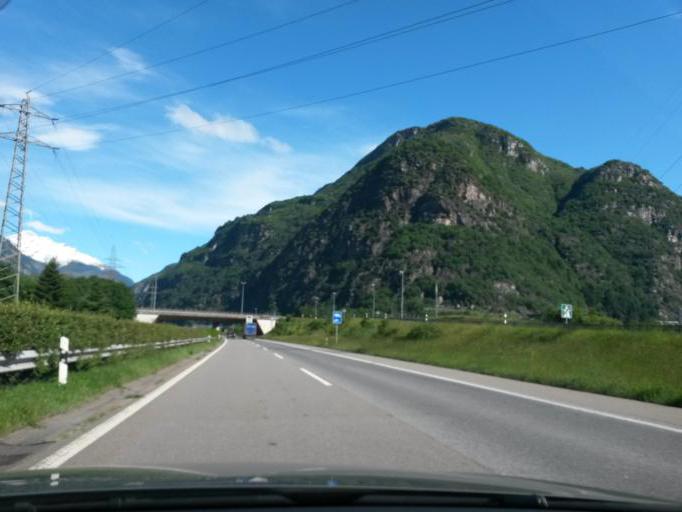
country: CH
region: Ticino
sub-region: Riviera District
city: Biasca
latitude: 46.3535
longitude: 8.9595
